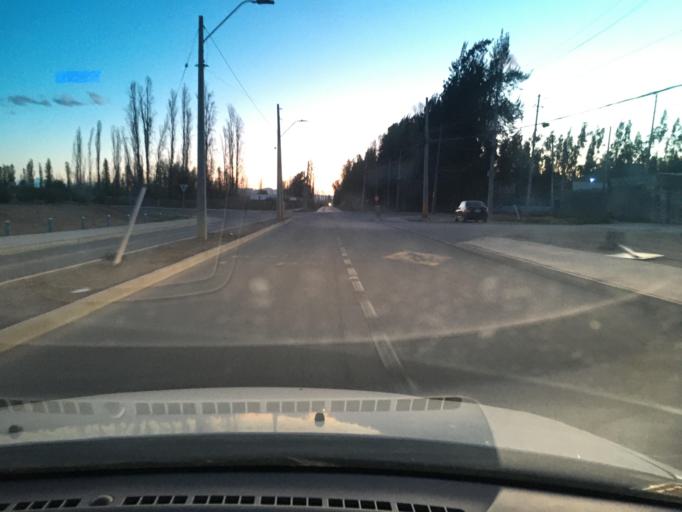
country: CL
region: Santiago Metropolitan
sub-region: Provincia de Chacabuco
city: Chicureo Abajo
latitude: -33.2908
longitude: -70.7367
